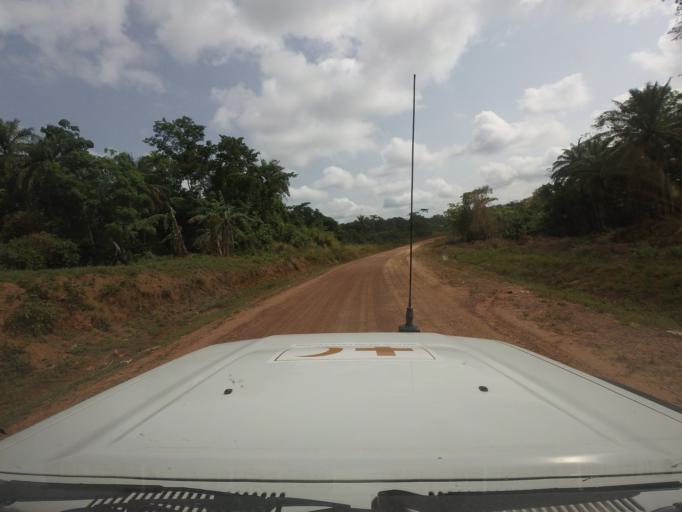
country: LR
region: Bong
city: Gbarnga
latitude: 7.2425
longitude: -9.4386
